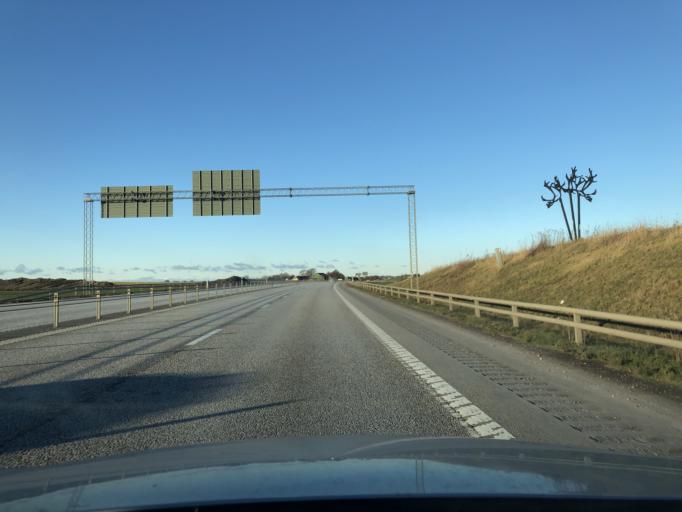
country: SE
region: Skane
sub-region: Trelleborgs Kommun
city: Skare
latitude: 55.3882
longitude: 13.0778
